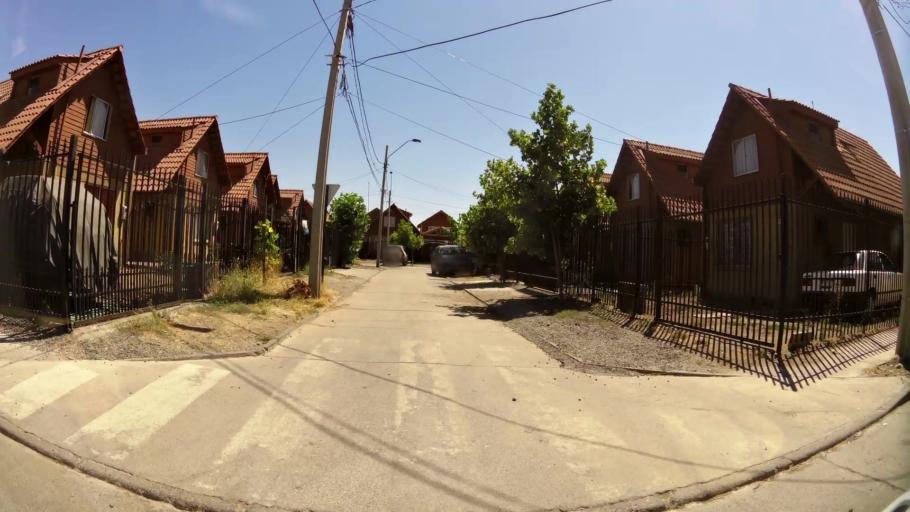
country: CL
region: Maule
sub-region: Provincia de Curico
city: Curico
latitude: -34.9658
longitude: -71.2303
